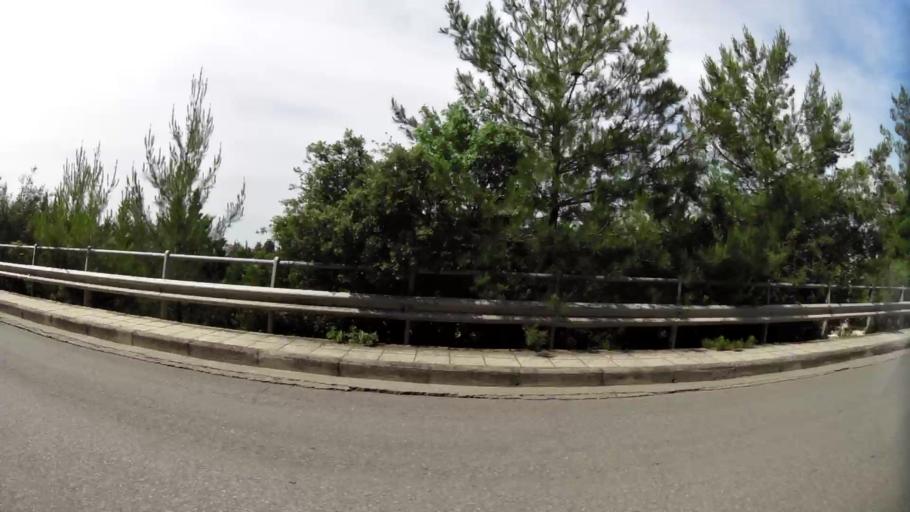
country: GR
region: Central Macedonia
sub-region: Nomos Thessalonikis
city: Panorama
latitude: 40.5862
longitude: 23.0219
